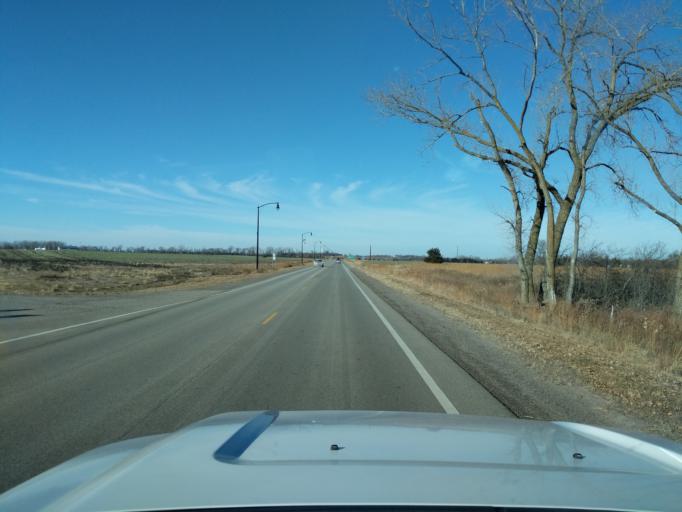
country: US
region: Minnesota
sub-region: Yellow Medicine County
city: Granite Falls
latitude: 44.7675
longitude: -95.5371
